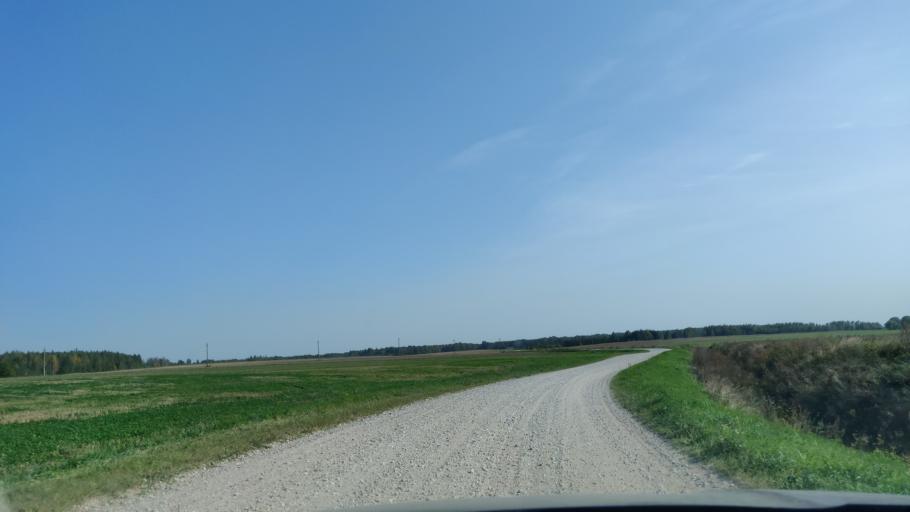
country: LT
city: Sirvintos
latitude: 54.9696
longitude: 24.8409
